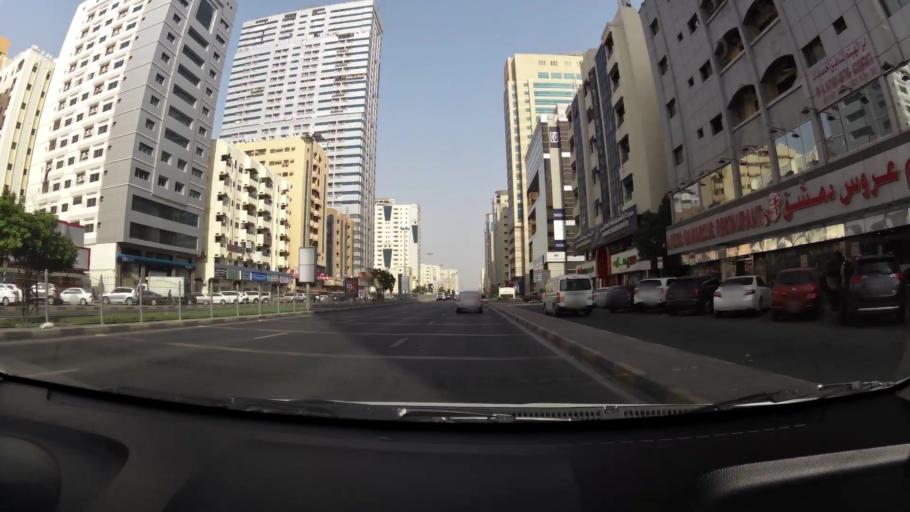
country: AE
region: Ash Shariqah
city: Sharjah
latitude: 25.3465
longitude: 55.3905
